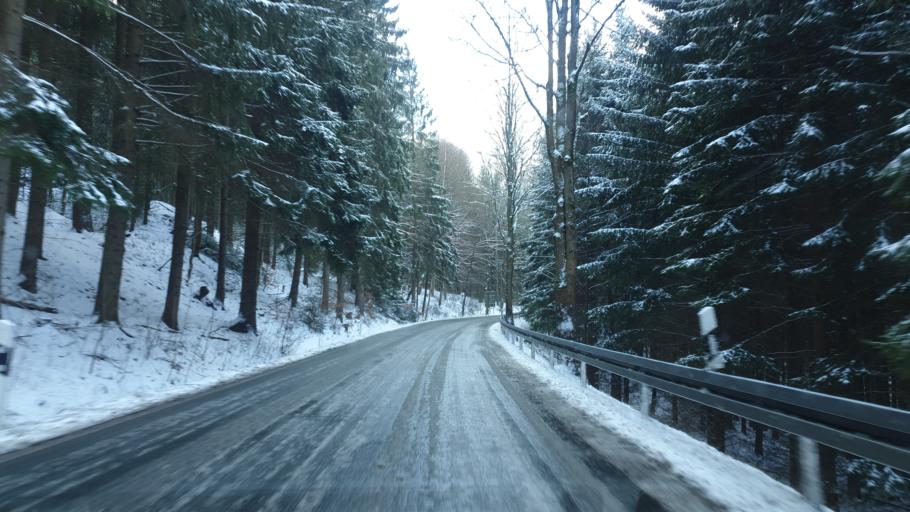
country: DE
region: Saxony
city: Bad Elster
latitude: 50.2704
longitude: 12.2502
